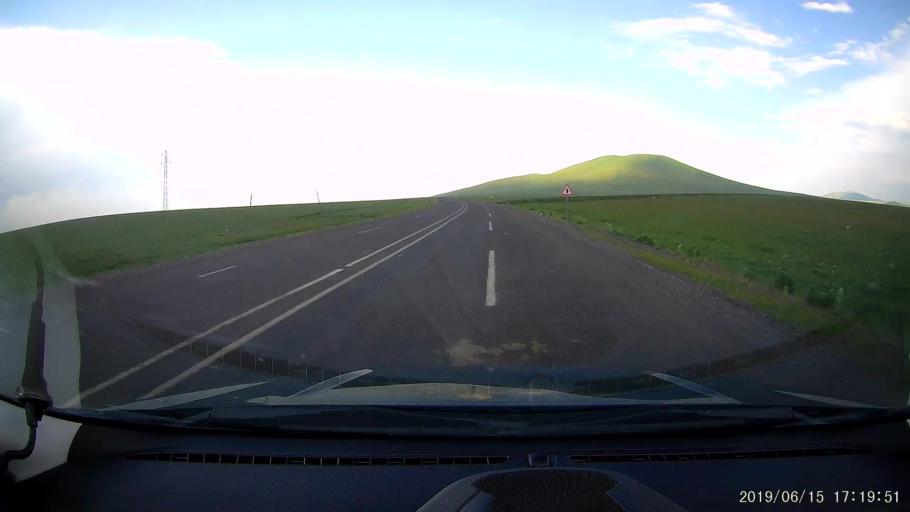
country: TR
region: Kars
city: Kars
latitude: 40.6161
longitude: 43.2877
